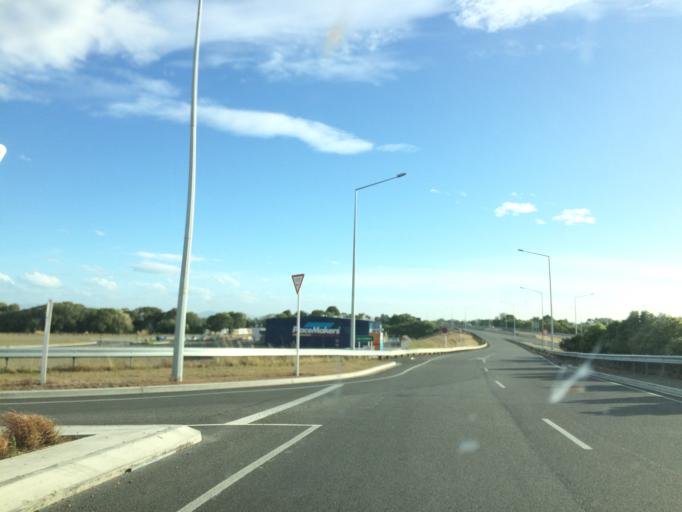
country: NZ
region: Canterbury
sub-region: Waimakariri District
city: Kaiapoi
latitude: -43.3747
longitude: 172.6471
